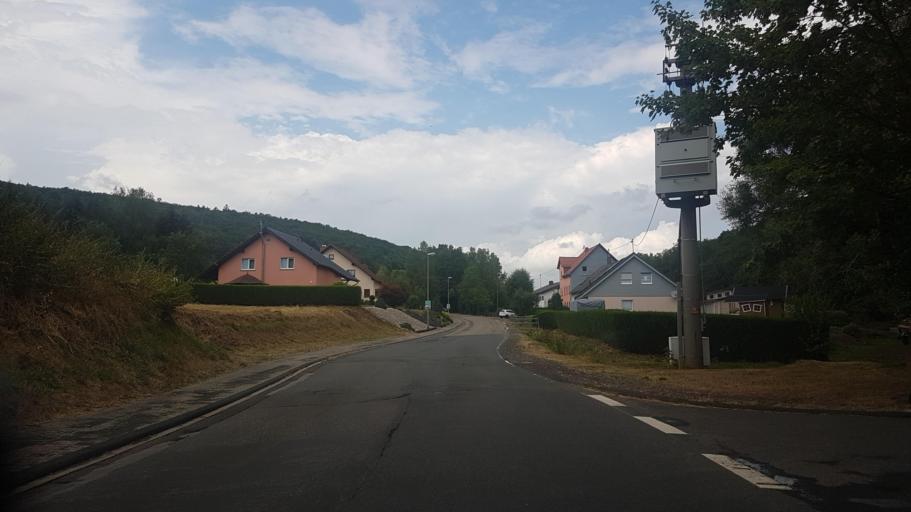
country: DE
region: Rheinland-Pfalz
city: Hoppstadten-Weiersbach
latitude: 49.6228
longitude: 7.1953
